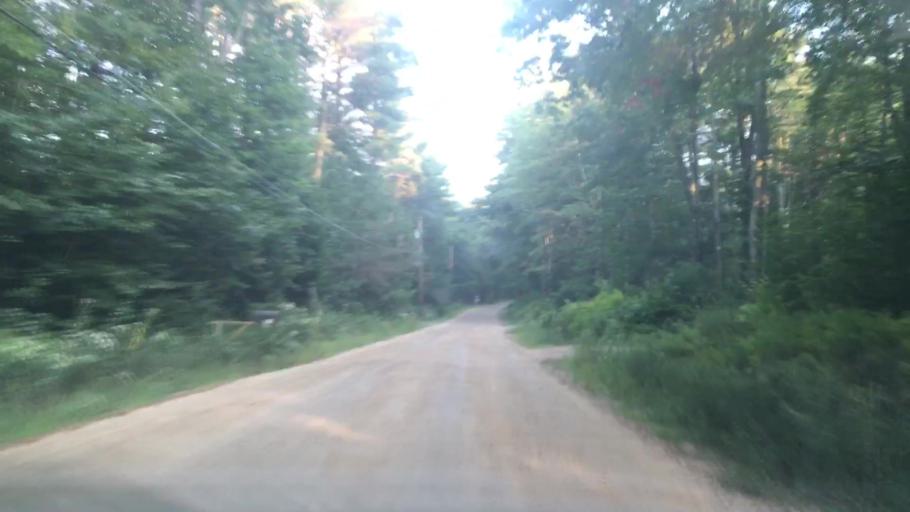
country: US
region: New Hampshire
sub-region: Belknap County
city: Barnstead
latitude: 43.4169
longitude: -71.2863
